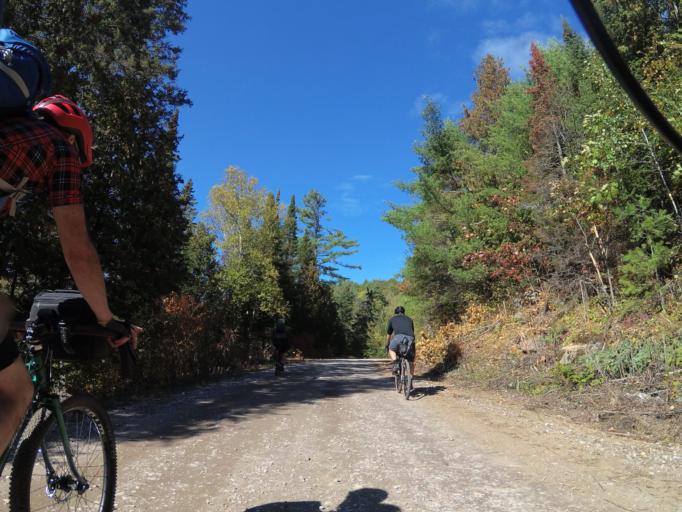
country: CA
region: Ontario
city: Renfrew
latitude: 45.3238
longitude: -77.0405
